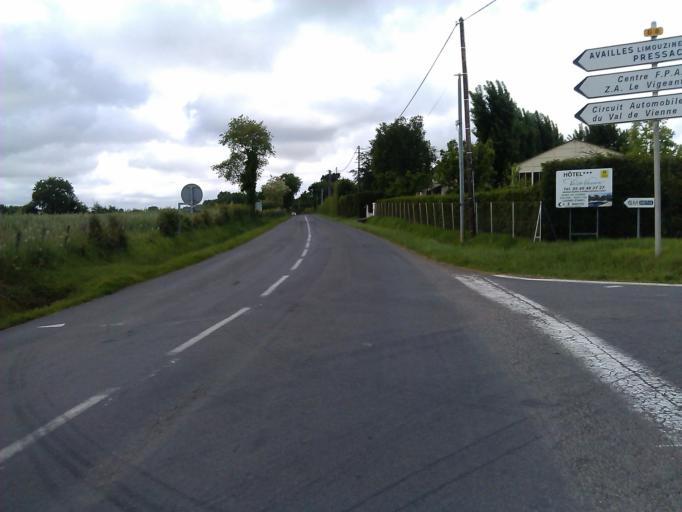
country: FR
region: Poitou-Charentes
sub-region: Departement de la Vienne
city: Availles-Limouzine
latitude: 46.2273
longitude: 0.6679
